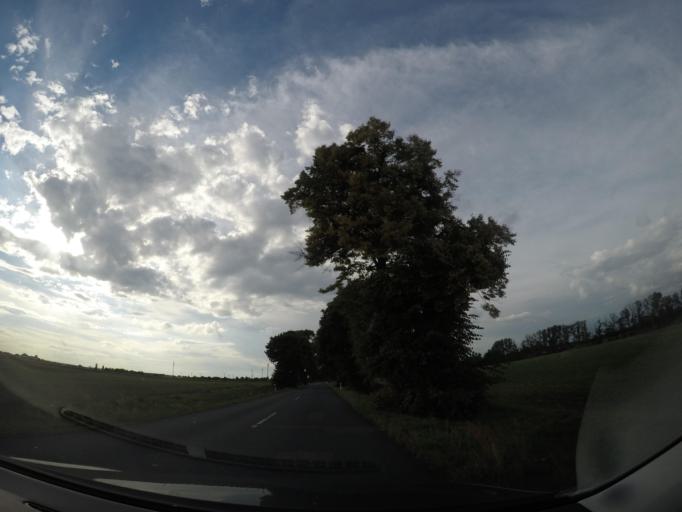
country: DE
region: Saxony-Anhalt
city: Kusey
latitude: 52.5777
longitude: 11.1093
